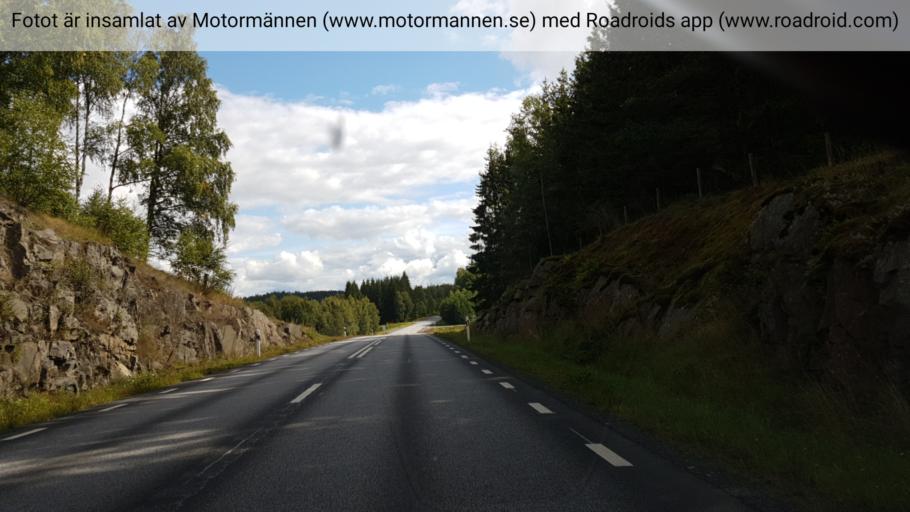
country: SE
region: Joenkoeping
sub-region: Jonkopings Kommun
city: Huskvarna
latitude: 57.7786
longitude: 14.3418
